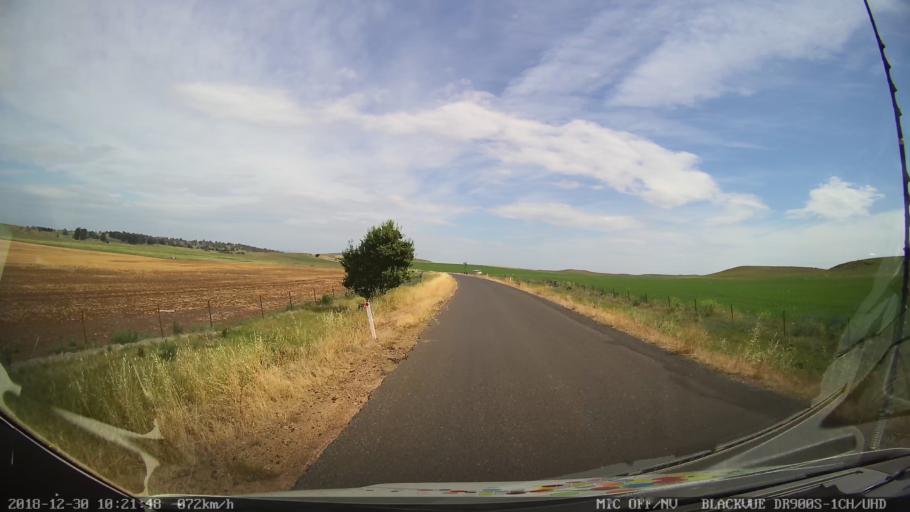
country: AU
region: New South Wales
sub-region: Snowy River
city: Berridale
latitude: -36.5489
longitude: 149.0024
